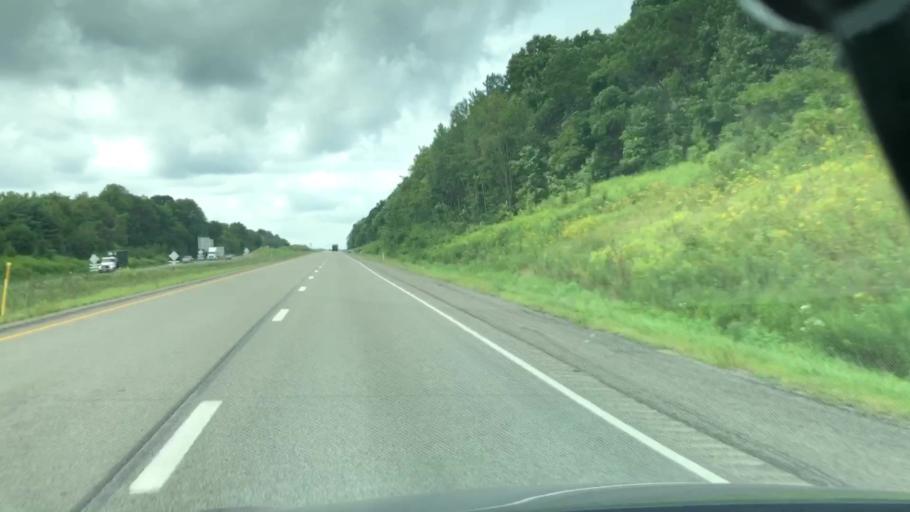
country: US
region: Pennsylvania
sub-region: Crawford County
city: Meadville
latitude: 41.6345
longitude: -80.1938
